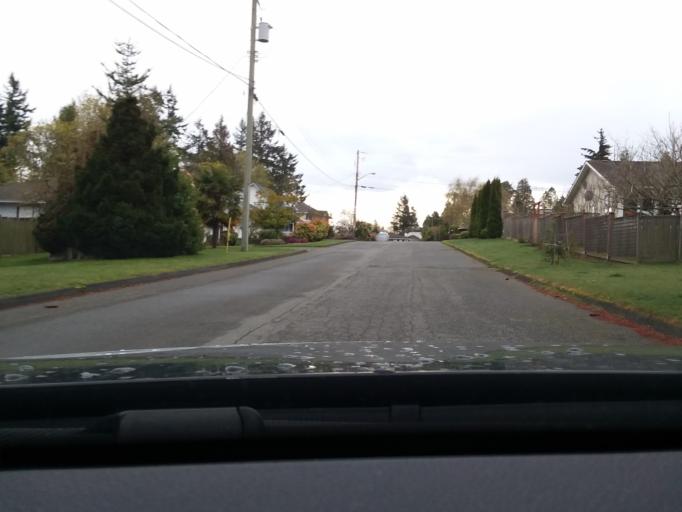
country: CA
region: British Columbia
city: Victoria
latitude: 48.5217
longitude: -123.3814
